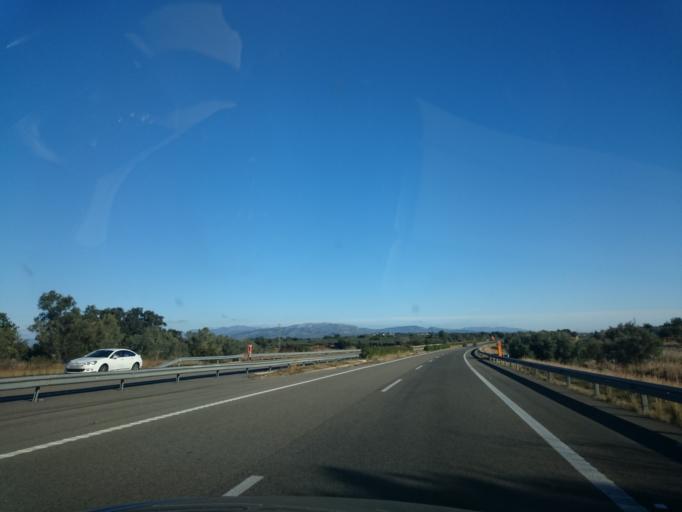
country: ES
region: Catalonia
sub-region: Provincia de Tarragona
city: Masdenverge
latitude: 40.6896
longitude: 0.5288
